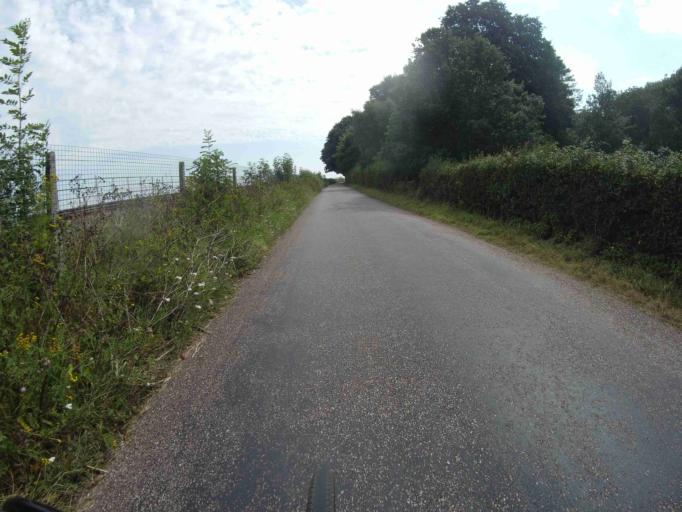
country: GB
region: England
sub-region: Devon
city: Starcross
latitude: 50.6362
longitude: -3.4501
